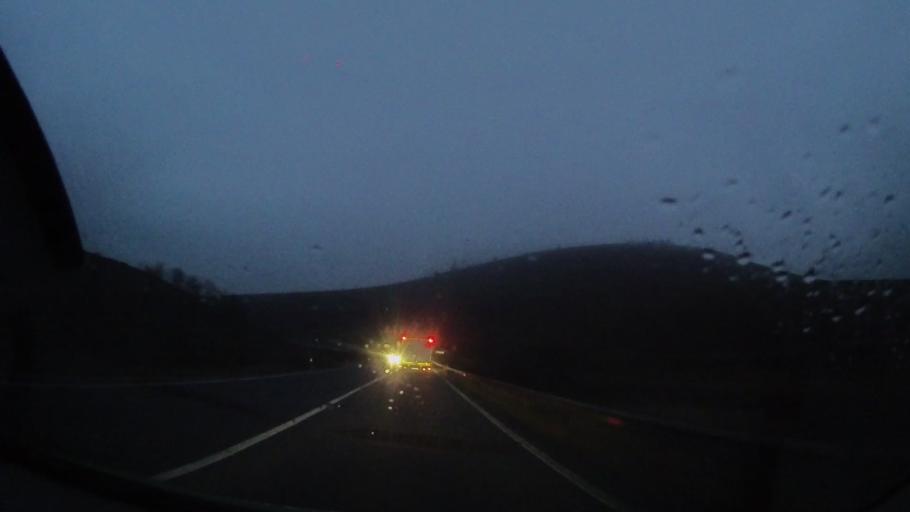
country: RO
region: Harghita
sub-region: Comuna Subcetate
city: Subcetate
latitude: 46.8387
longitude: 25.4840
